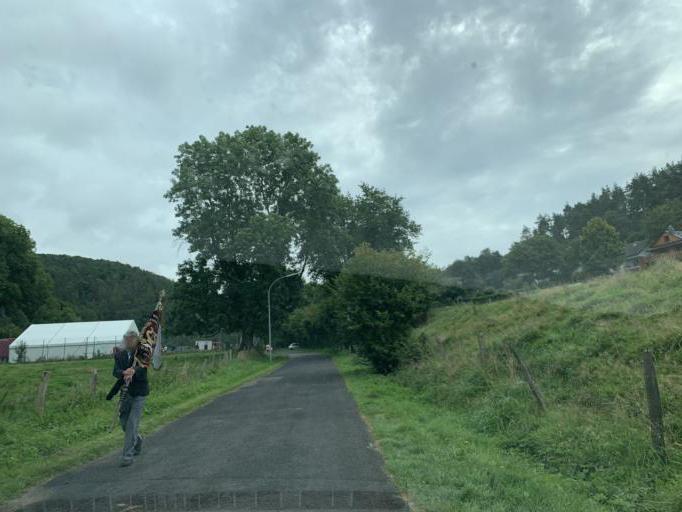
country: DE
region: North Rhine-Westphalia
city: Heimbach
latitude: 50.6512
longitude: 6.4956
